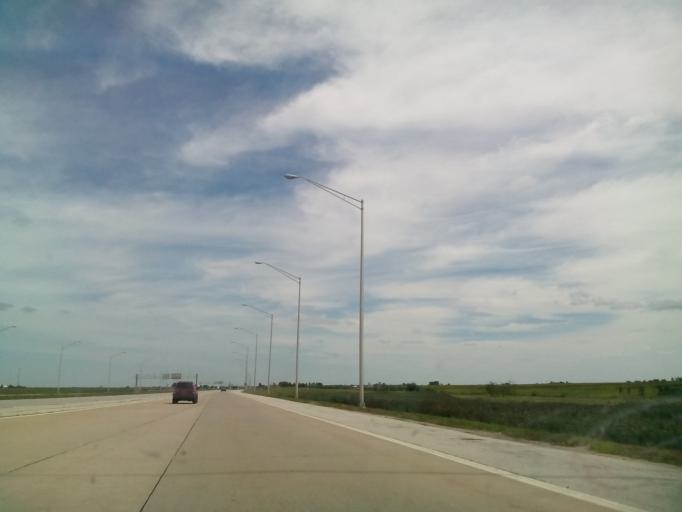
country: US
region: Illinois
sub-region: DeKalb County
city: Malta
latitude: 41.8994
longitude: -88.8732
